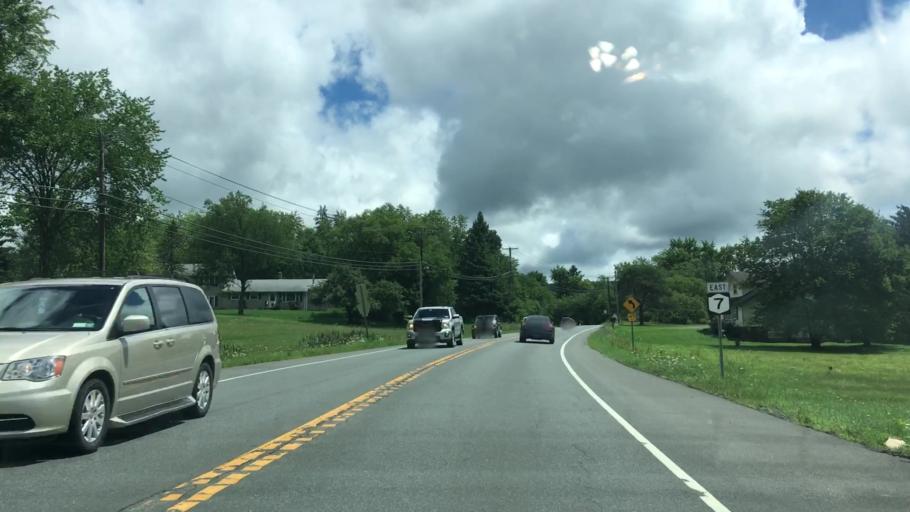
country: US
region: New York
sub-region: Rensselaer County
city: Hoosick Falls
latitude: 42.8452
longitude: -73.4584
